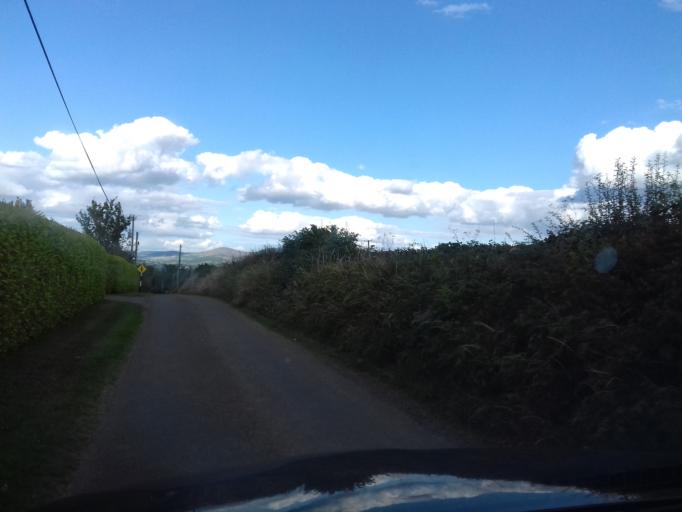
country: IE
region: Leinster
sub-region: Kilkenny
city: Graiguenamanagh
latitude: 52.5872
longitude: -6.9998
